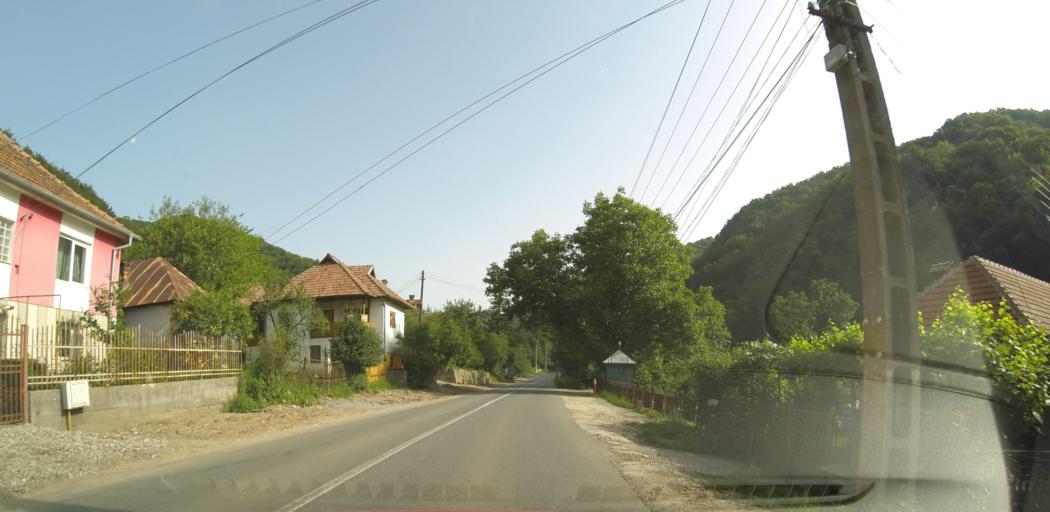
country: RO
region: Valcea
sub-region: Oras Baile Olanesti
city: Olanesti
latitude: 45.1898
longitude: 24.2518
